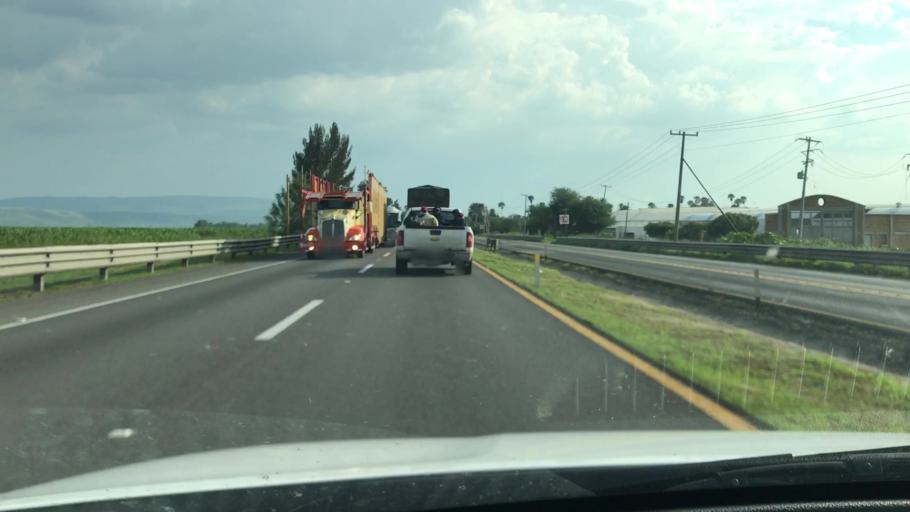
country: MX
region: Guanajuato
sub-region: Irapuato
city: San Ignacio de Rivera (Ojo de Agua)
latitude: 20.5131
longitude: -101.4688
